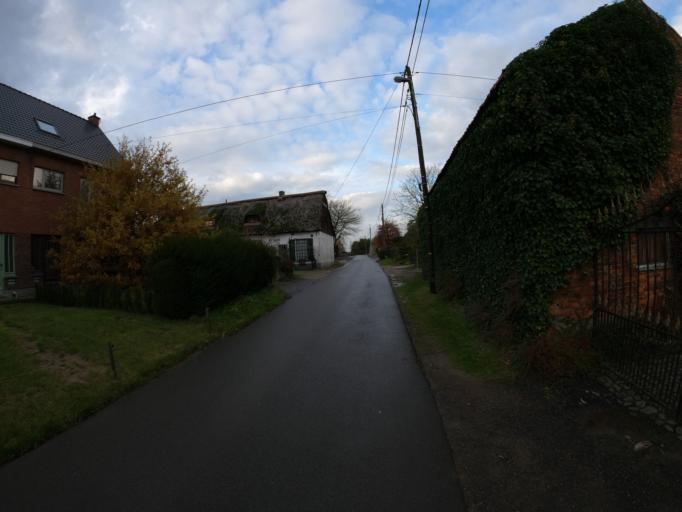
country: BE
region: Flanders
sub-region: Provincie Oost-Vlaanderen
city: Hamme
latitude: 51.1176
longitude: 4.1587
